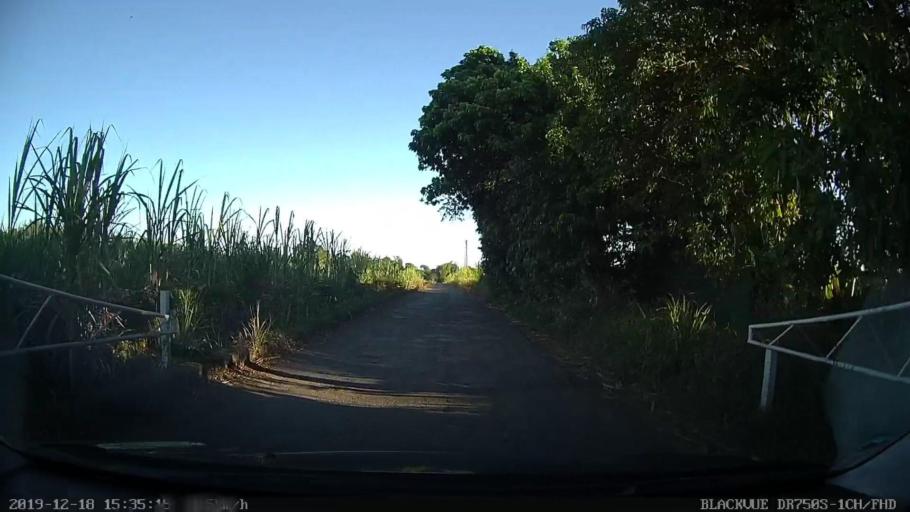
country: RE
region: Reunion
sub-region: Reunion
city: Bras-Panon
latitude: -20.9984
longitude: 55.6619
